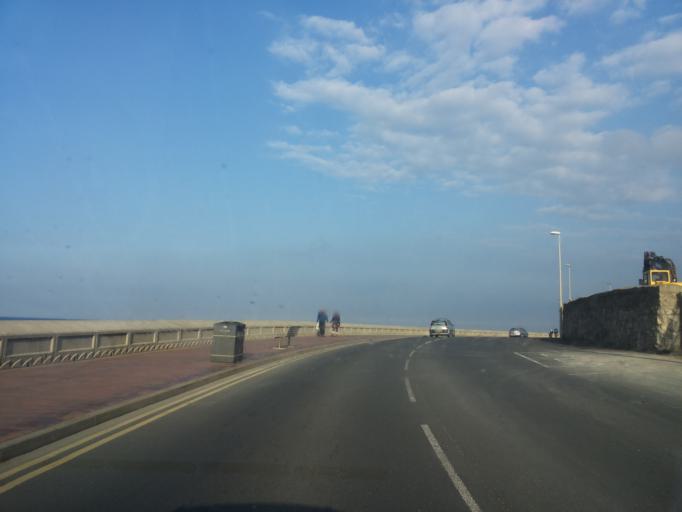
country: GB
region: England
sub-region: North Yorkshire
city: Scarborough
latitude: 54.2903
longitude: -0.3898
